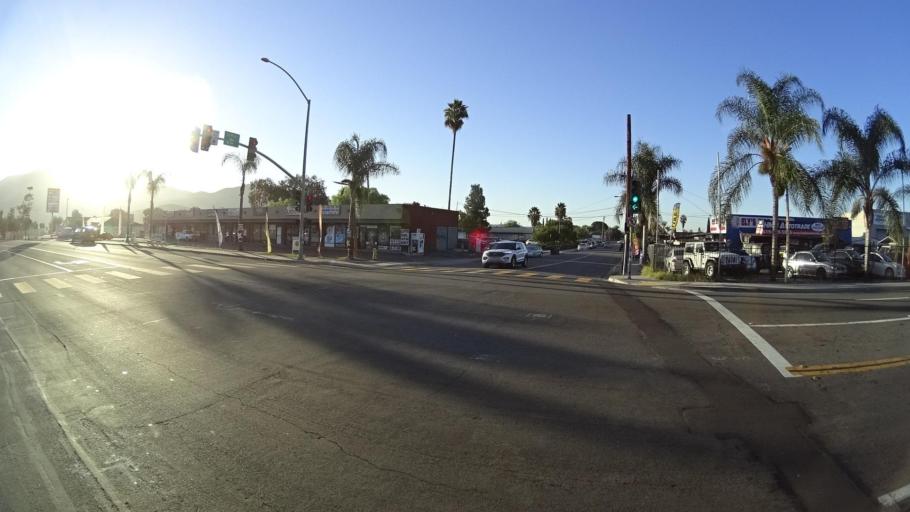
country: US
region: California
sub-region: San Diego County
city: La Presa
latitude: 32.7078
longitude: -116.9933
